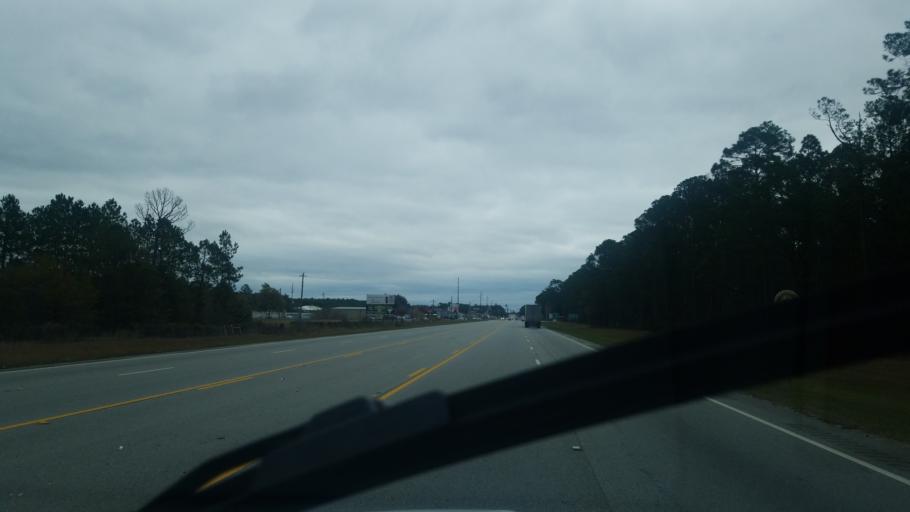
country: US
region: Georgia
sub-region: Ware County
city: Deenwood
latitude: 31.2088
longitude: -82.3929
